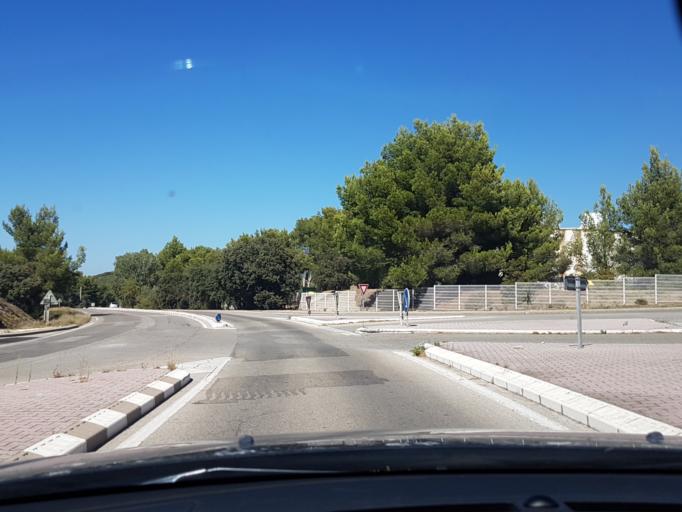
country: FR
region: Provence-Alpes-Cote d'Azur
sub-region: Departement des Bouches-du-Rhone
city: Orgon
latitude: 43.7862
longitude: 5.0254
